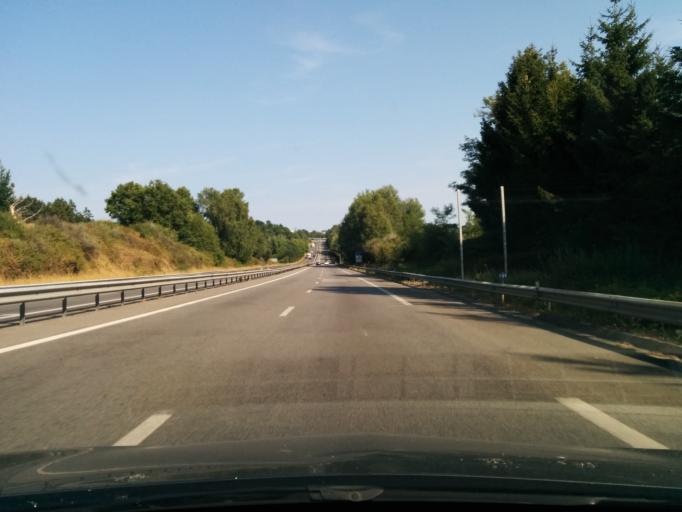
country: FR
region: Limousin
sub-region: Departement de la Haute-Vienne
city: Boisseuil
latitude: 45.7719
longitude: 1.3134
